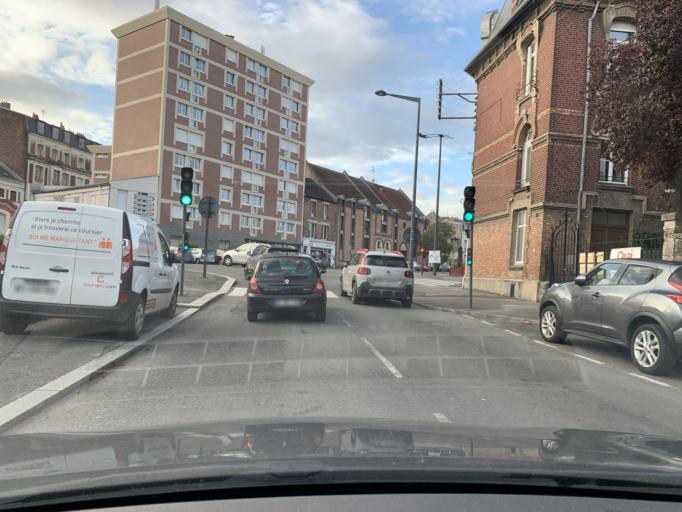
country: FR
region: Picardie
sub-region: Departement de l'Aisne
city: Saint-Quentin
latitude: 49.8431
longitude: 3.2955
